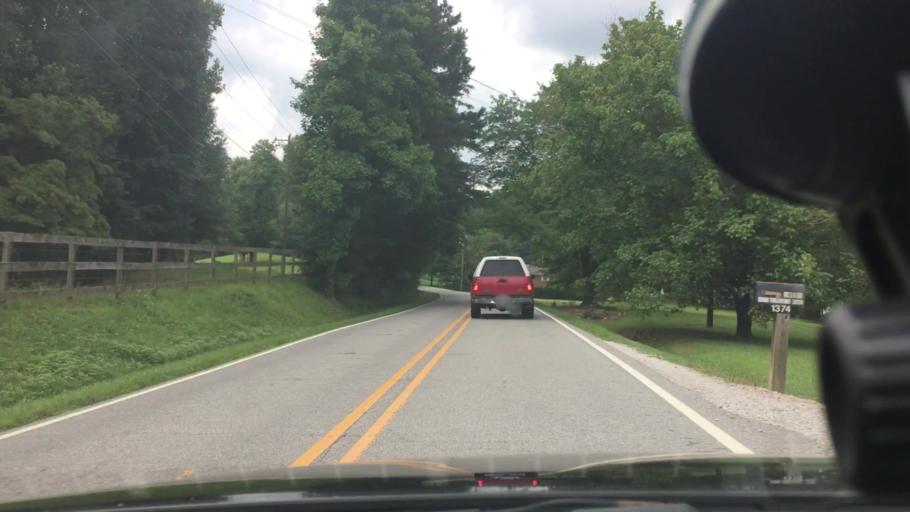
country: US
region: North Carolina
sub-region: McDowell County
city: West Marion
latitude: 35.6459
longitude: -82.0156
